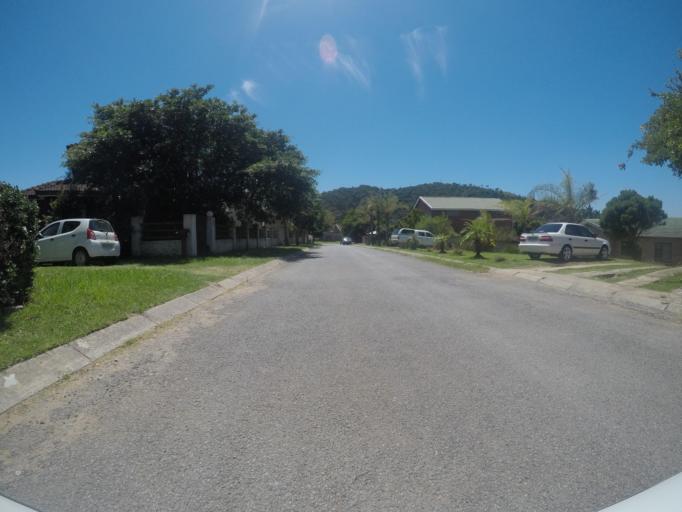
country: ZA
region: Eastern Cape
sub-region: Buffalo City Metropolitan Municipality
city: East London
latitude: -32.9284
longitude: 27.9971
